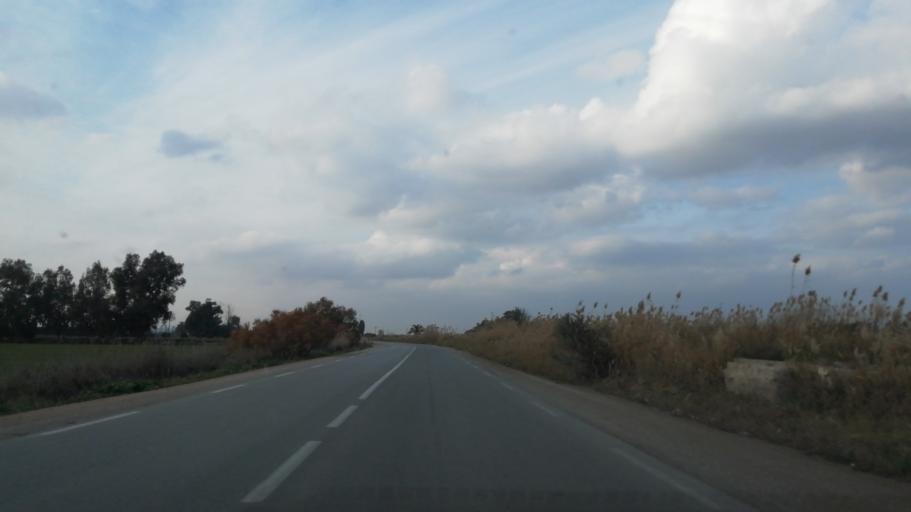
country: DZ
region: Mascara
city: Sig
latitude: 35.6488
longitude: 0.0243
